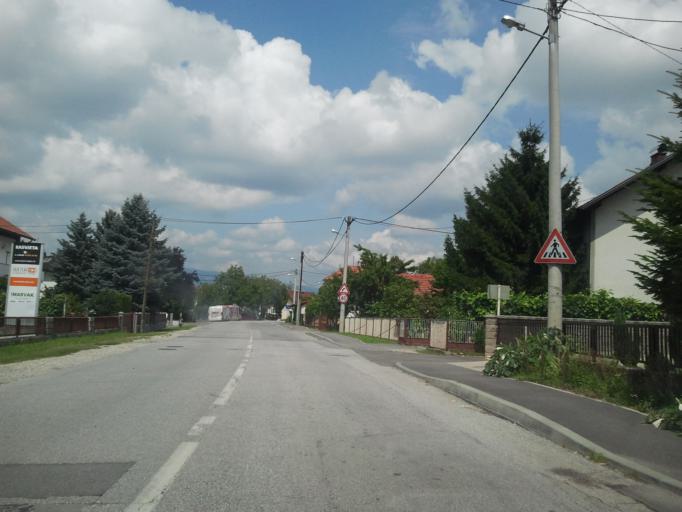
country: HR
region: Grad Zagreb
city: Zadvorsko
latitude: 45.7615
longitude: 15.9155
